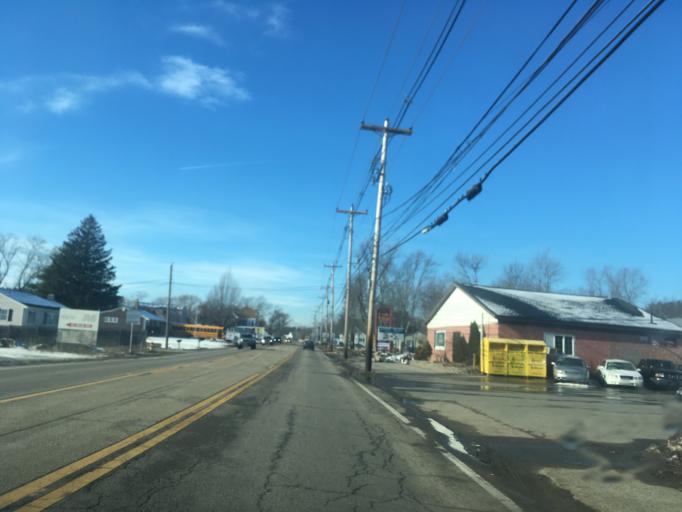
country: US
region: Massachusetts
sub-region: Essex County
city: Salisbury
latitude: 42.8406
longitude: -70.8673
